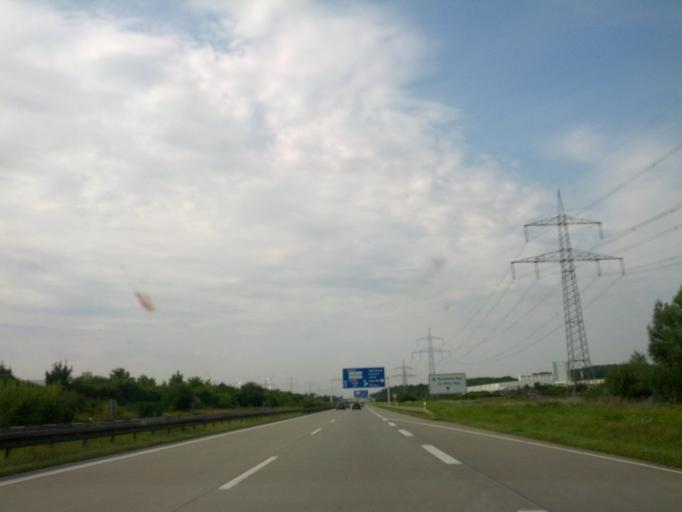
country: DE
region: Mecklenburg-Vorpommern
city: Kavelstorf
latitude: 54.0135
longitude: 12.2027
